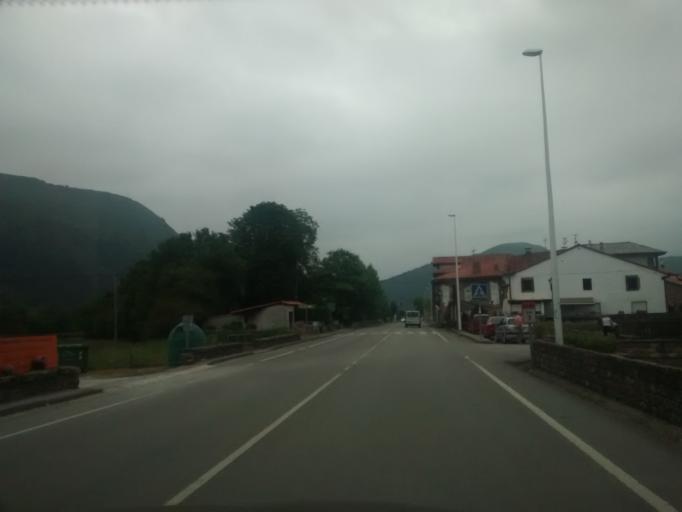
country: ES
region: Cantabria
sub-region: Provincia de Cantabria
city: Ruente
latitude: 43.2595
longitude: -4.2666
